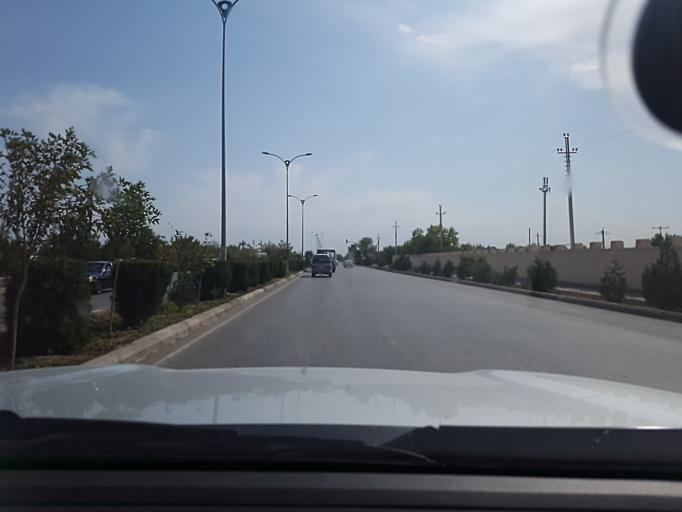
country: TM
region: Dasoguz
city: Dasoguz
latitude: 41.8573
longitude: 59.9424
